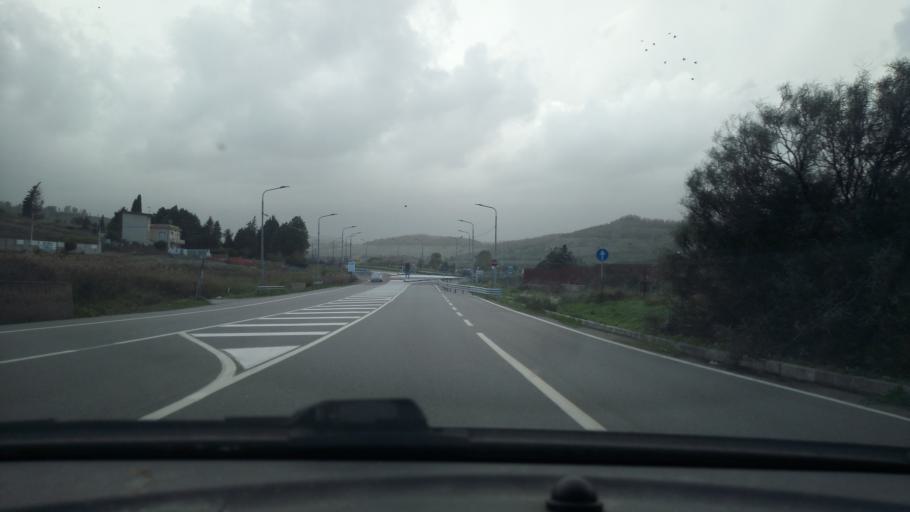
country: IT
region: Calabria
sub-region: Provincia di Catanzaro
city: Barone
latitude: 38.8611
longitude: 16.6309
